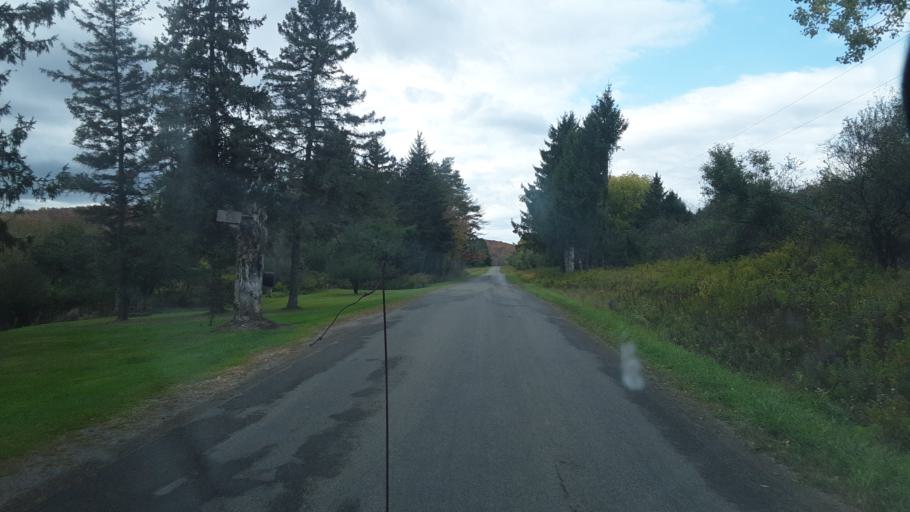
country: US
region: New York
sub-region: Allegany County
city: Alfred
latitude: 42.3645
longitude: -77.8248
